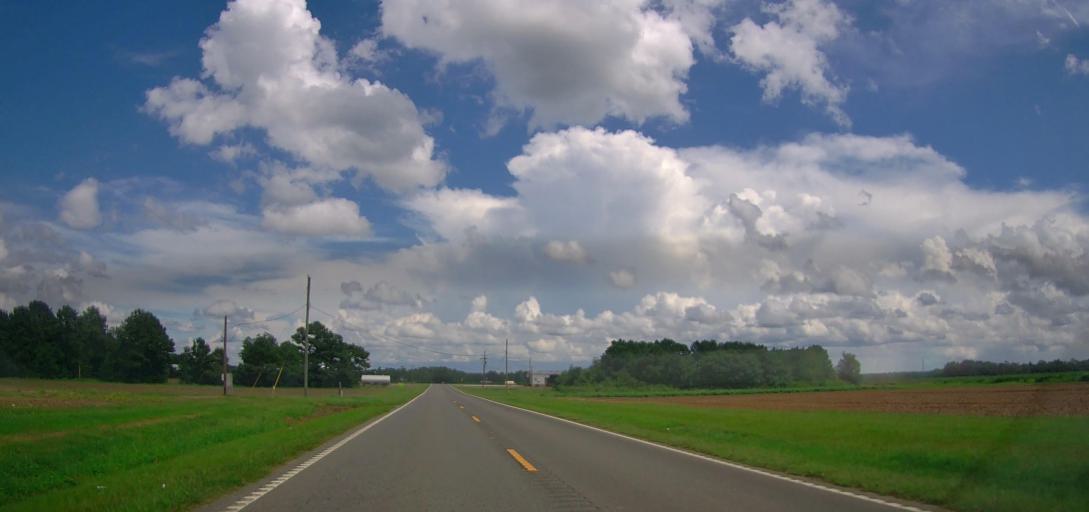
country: US
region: Georgia
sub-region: Taylor County
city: Reynolds
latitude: 32.4400
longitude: -84.0856
